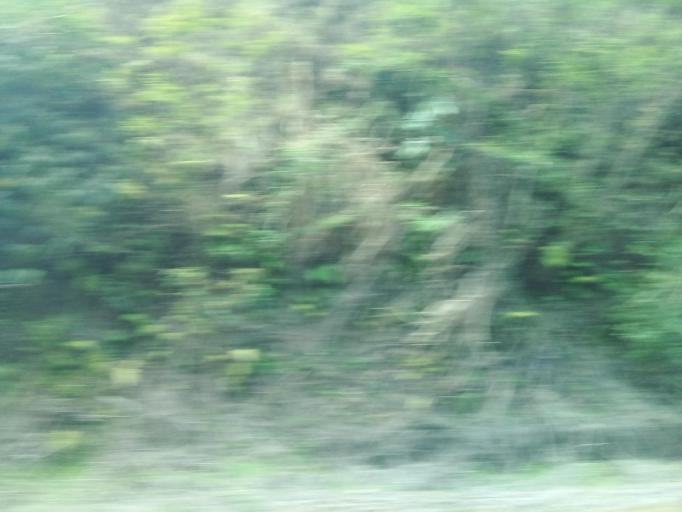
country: BR
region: Minas Gerais
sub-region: Governador Valadares
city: Governador Valadares
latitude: -18.9253
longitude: -42.0188
